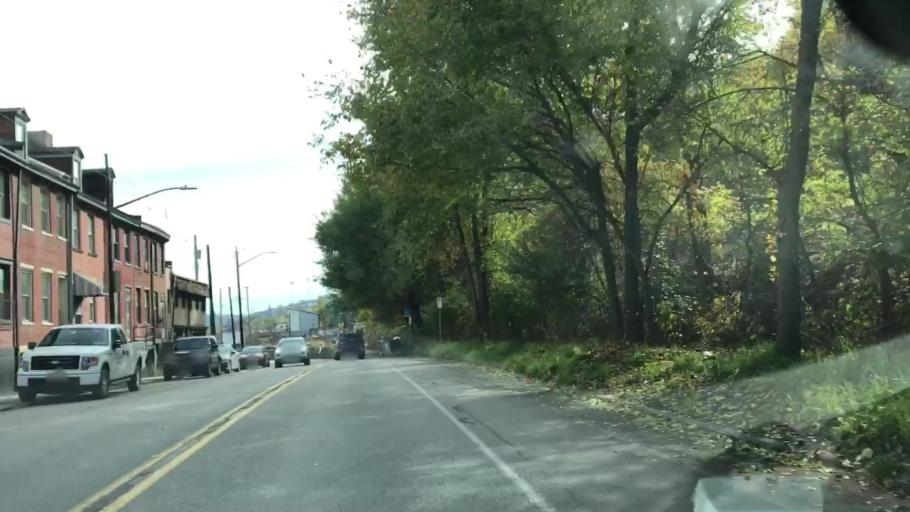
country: US
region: Pennsylvania
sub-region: Allegheny County
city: Pittsburgh
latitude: 40.4290
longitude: -79.9959
